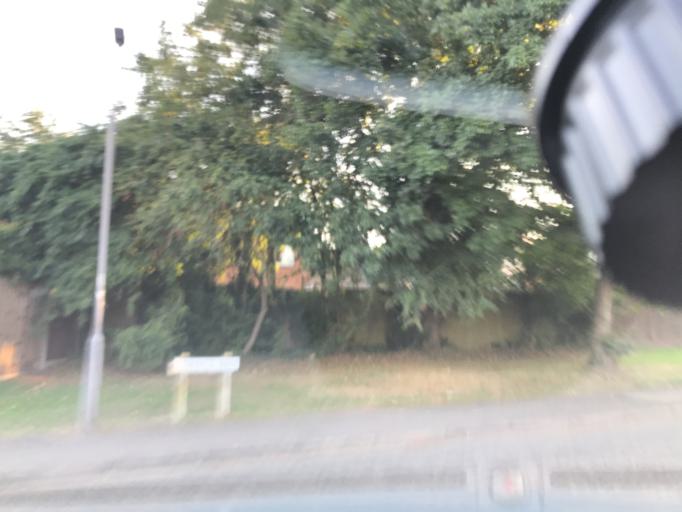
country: GB
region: England
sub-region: Buckinghamshire
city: Aylesbury
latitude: 51.8238
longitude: -0.7928
